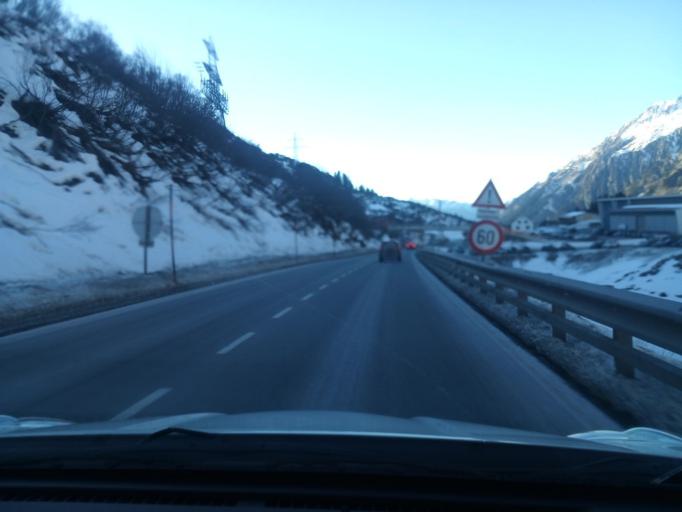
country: AT
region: Tyrol
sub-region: Politischer Bezirk Landeck
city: Sankt Anton am Arlberg
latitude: 47.1372
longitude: 10.1831
